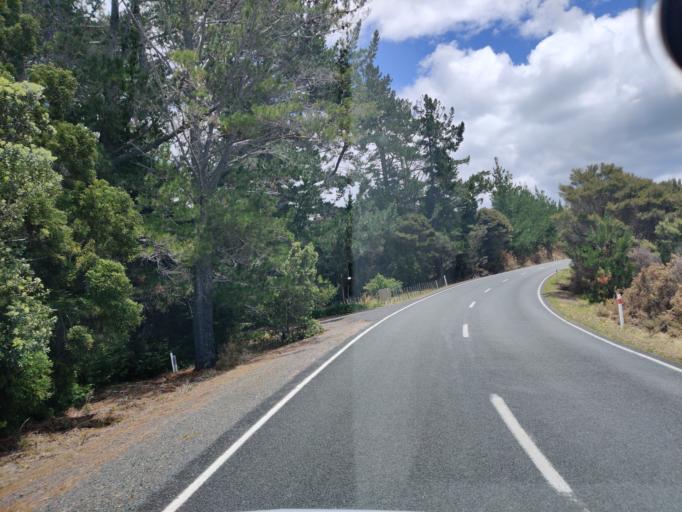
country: NZ
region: Northland
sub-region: Far North District
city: Paihia
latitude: -35.3043
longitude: 174.1301
